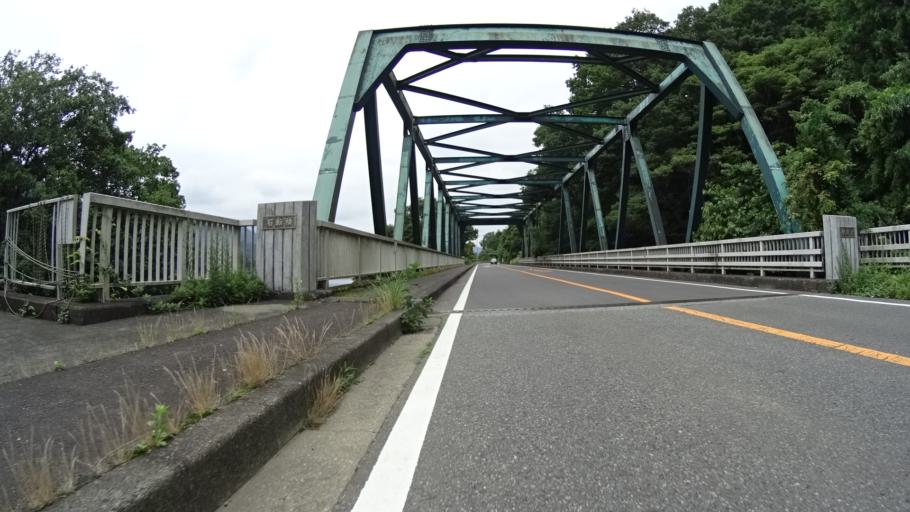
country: JP
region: Kanagawa
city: Atsugi
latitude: 35.5131
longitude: 139.2456
